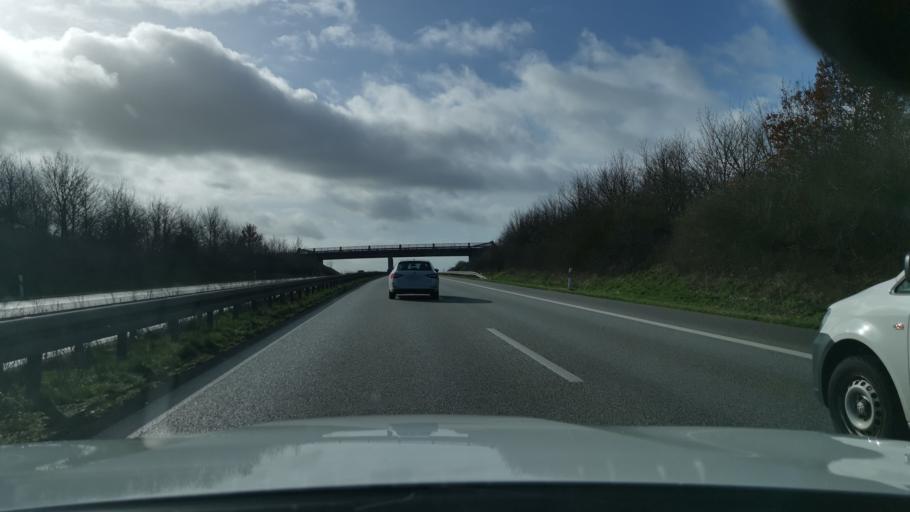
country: DE
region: Mecklenburg-Vorpommern
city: Kritzmow
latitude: 54.0668
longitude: 12.0490
